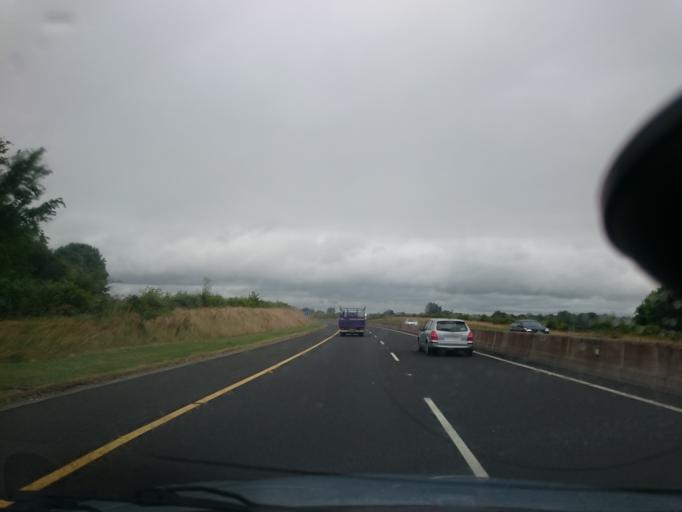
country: IE
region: Leinster
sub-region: Kildare
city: Castledermot
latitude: 52.9463
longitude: -6.8533
